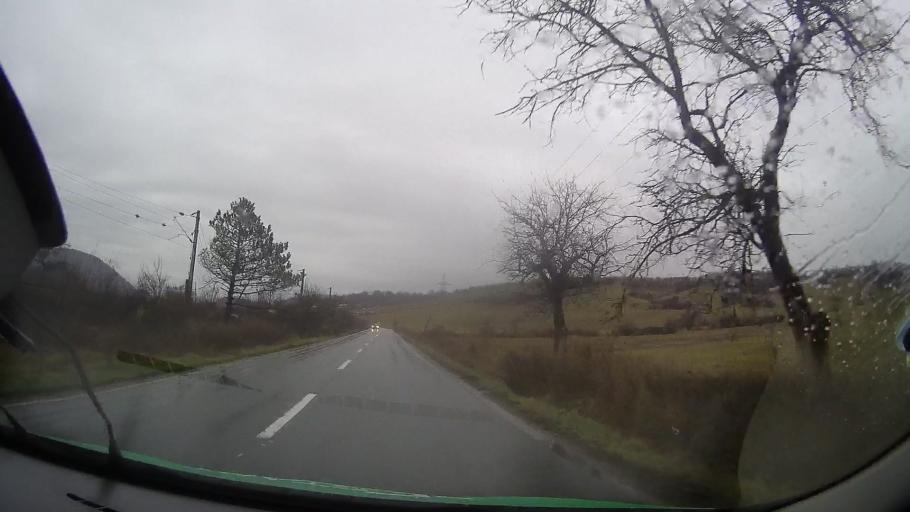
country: RO
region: Bistrita-Nasaud
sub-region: Municipiul Bistrita
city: Viisoara
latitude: 47.0464
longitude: 24.4640
